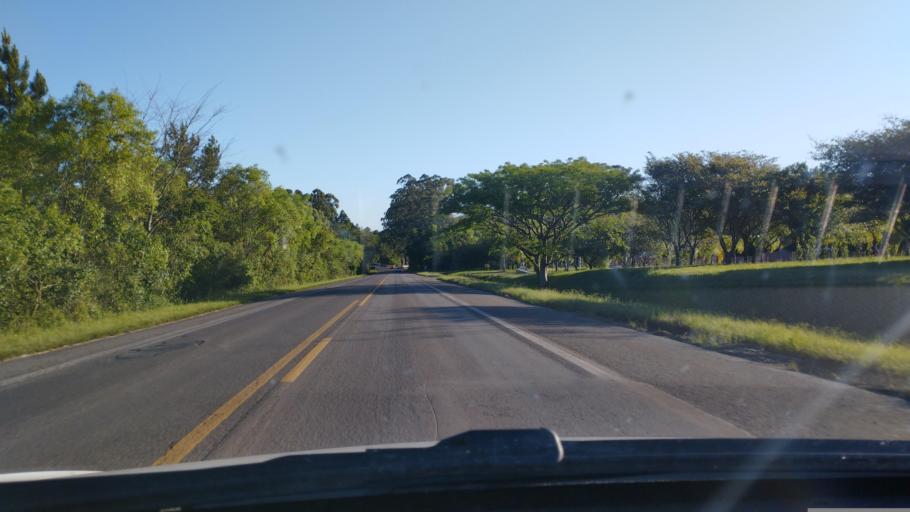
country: BR
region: Rio Grande do Sul
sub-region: Santa Maria
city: Santa Maria
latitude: -29.5944
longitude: -53.7666
